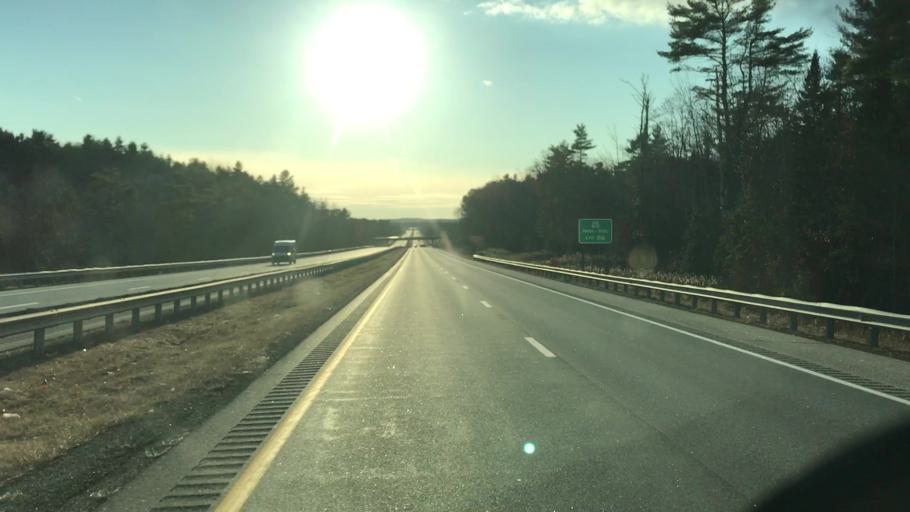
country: US
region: Maine
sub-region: Androscoggin County
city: Sabattus
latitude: 44.1158
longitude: -70.0566
